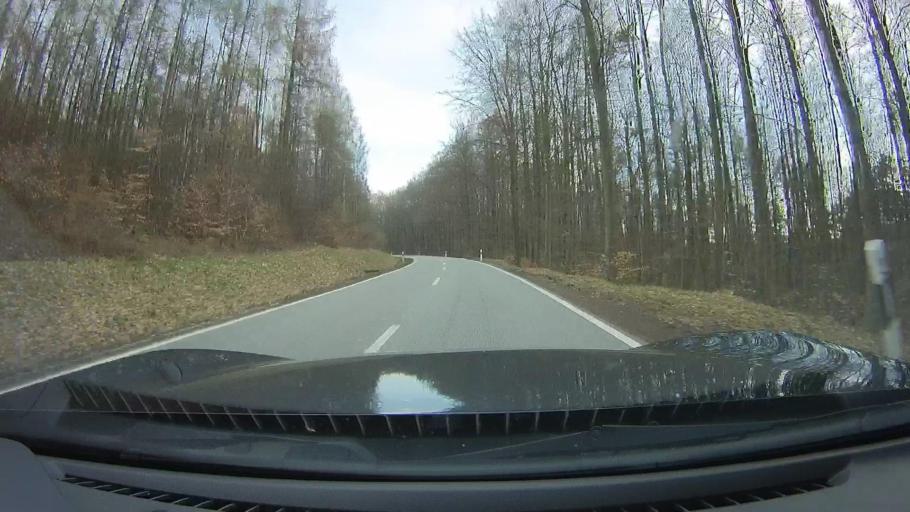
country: DE
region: Hesse
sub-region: Regierungsbezirk Darmstadt
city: Hesseneck
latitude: 49.5460
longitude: 9.1319
